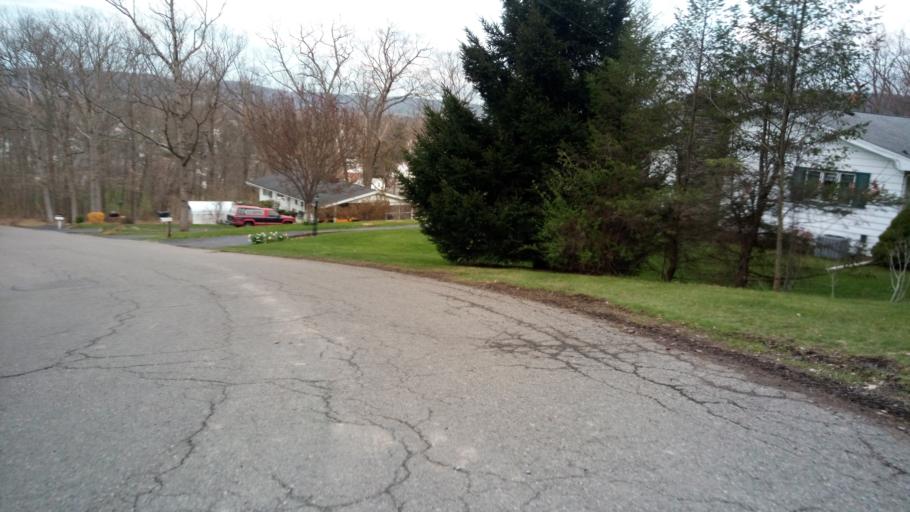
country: US
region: New York
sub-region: Chemung County
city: Southport
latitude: 42.0638
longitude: -76.8204
